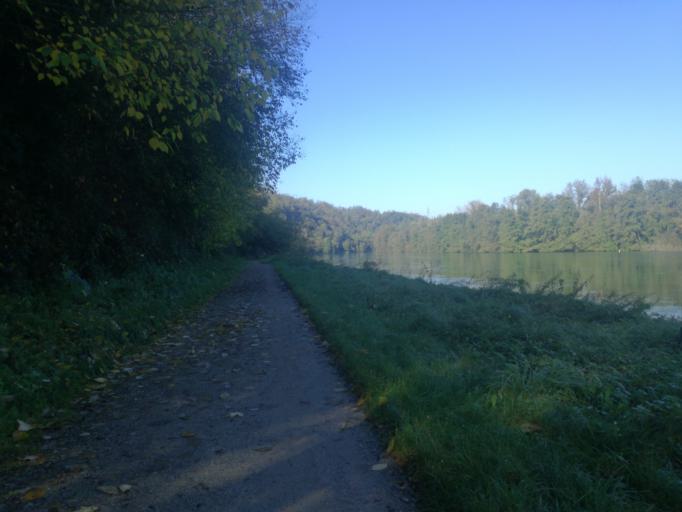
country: IT
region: Lombardy
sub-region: Provincia di Bergamo
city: Bottanuco
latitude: 45.6279
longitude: 9.5043
